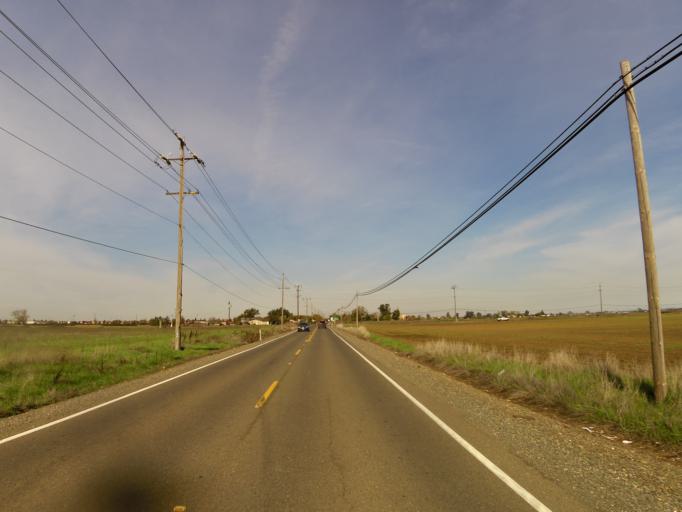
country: US
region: California
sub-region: Sacramento County
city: Laguna
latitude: 38.3702
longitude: -121.4176
